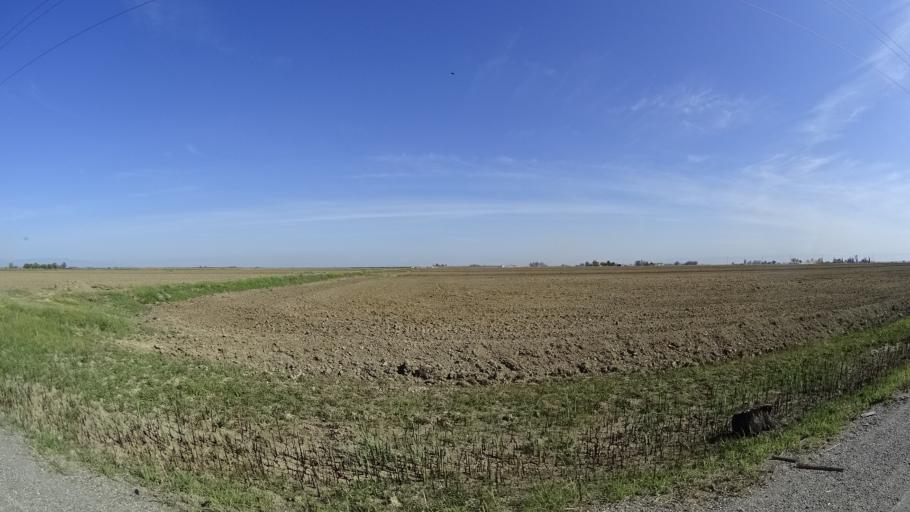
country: US
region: California
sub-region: Glenn County
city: Willows
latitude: 39.5532
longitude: -122.1222
